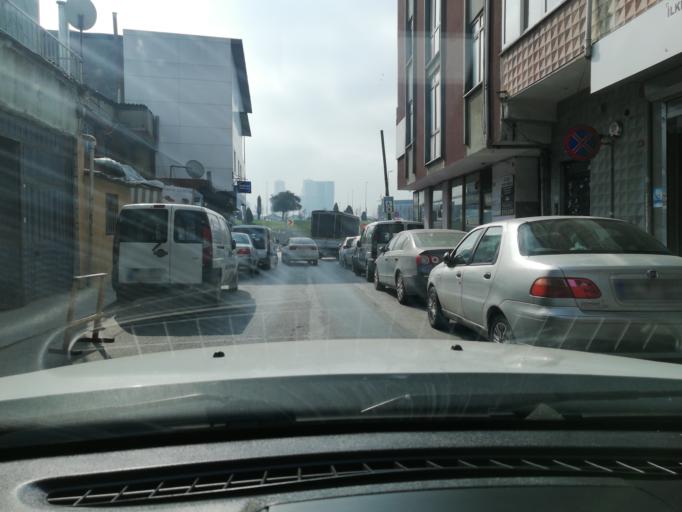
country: TR
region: Istanbul
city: Sisli
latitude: 41.0692
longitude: 28.9775
